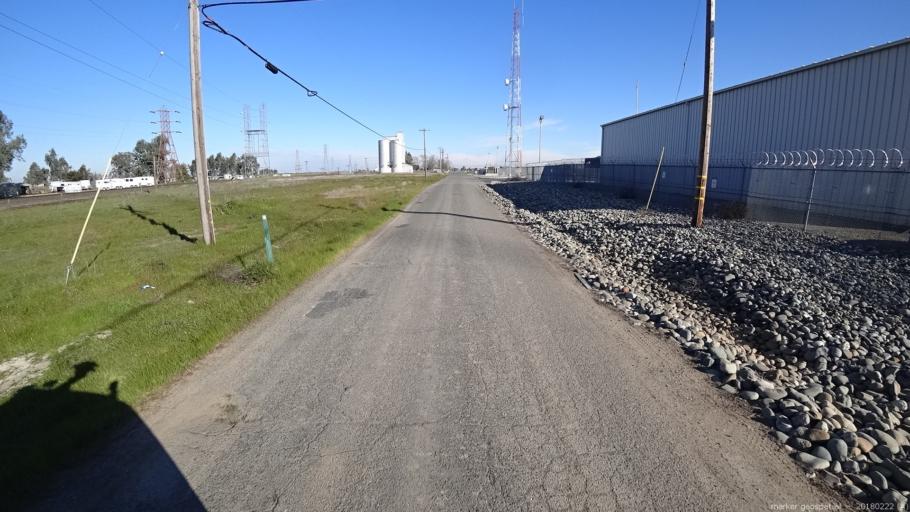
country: US
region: California
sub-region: Sacramento County
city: Elverta
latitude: 38.7119
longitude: -121.4845
